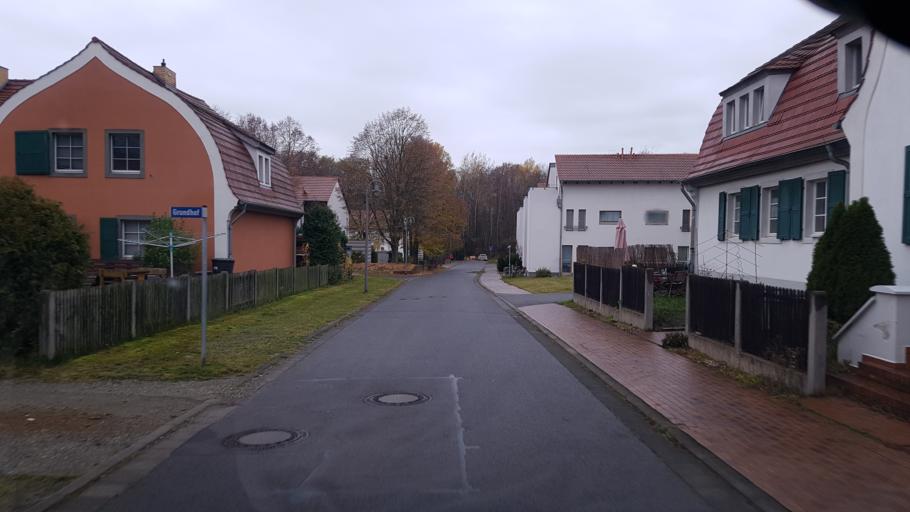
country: DE
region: Brandenburg
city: Lauchhammer
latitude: 51.4942
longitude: 13.7435
